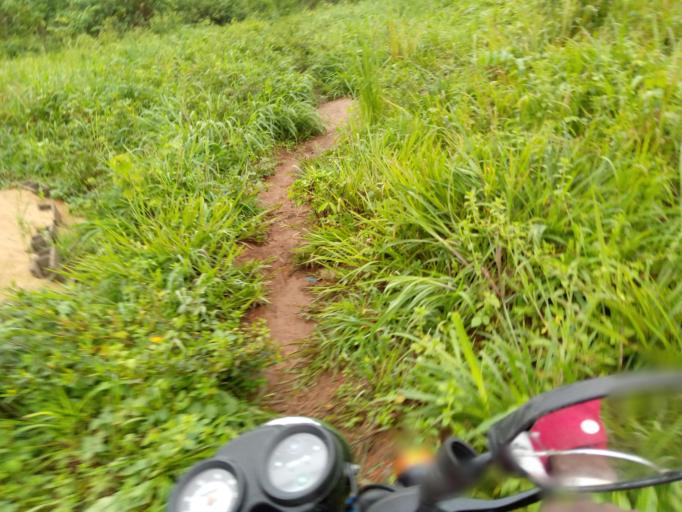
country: SL
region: Eastern Province
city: Buedu
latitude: 8.4688
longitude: -10.3450
